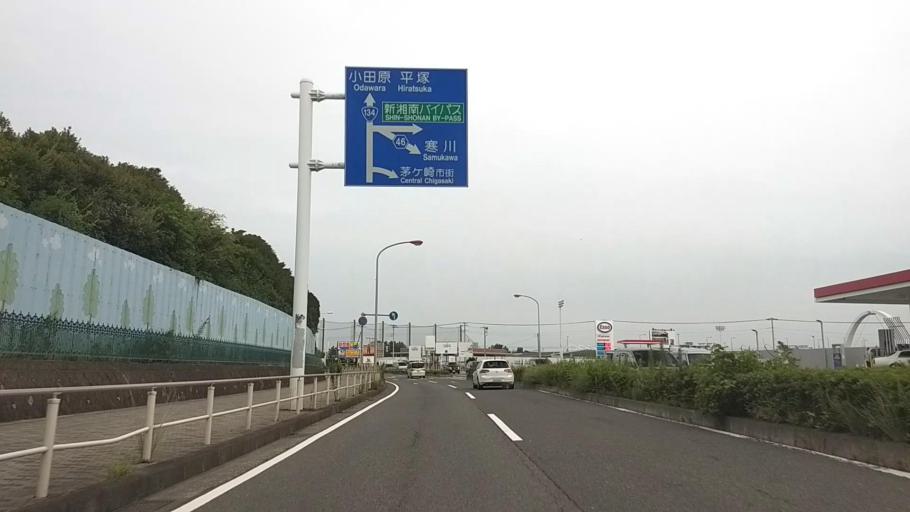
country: JP
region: Kanagawa
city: Chigasaki
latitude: 35.3194
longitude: 139.3787
